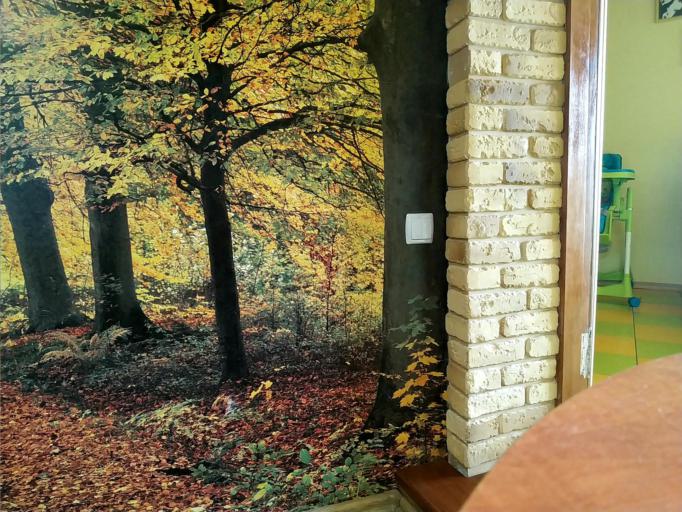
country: RU
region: Smolensk
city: Ozernyy
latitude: 55.4585
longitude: 32.6643
